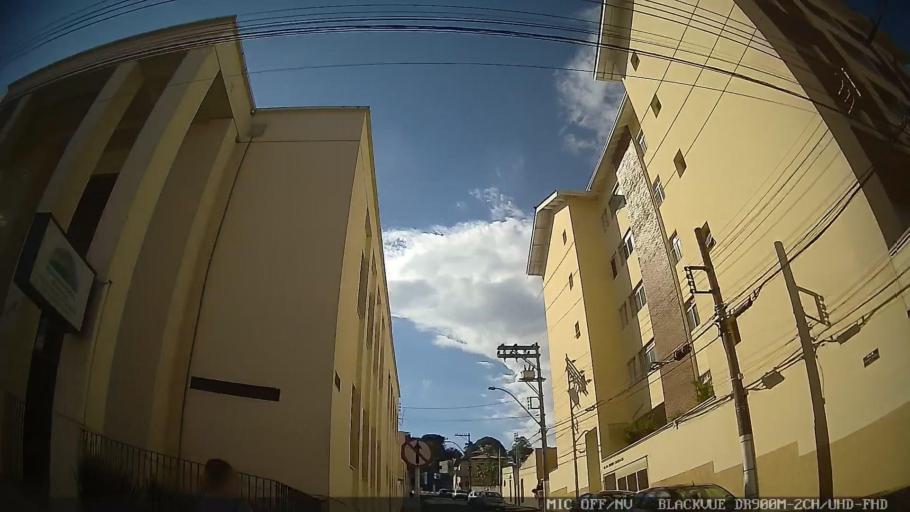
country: BR
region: Sao Paulo
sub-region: Serra Negra
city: Serra Negra
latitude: -22.6133
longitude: -46.7018
